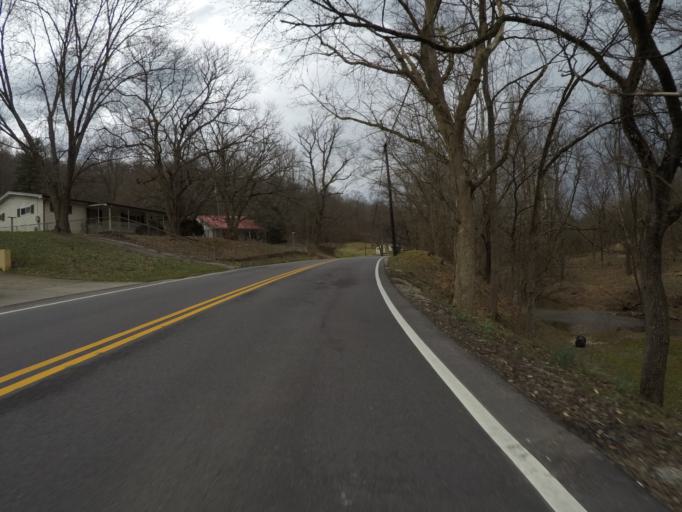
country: US
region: Ohio
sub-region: Lawrence County
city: Burlington
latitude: 38.4362
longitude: -82.4953
